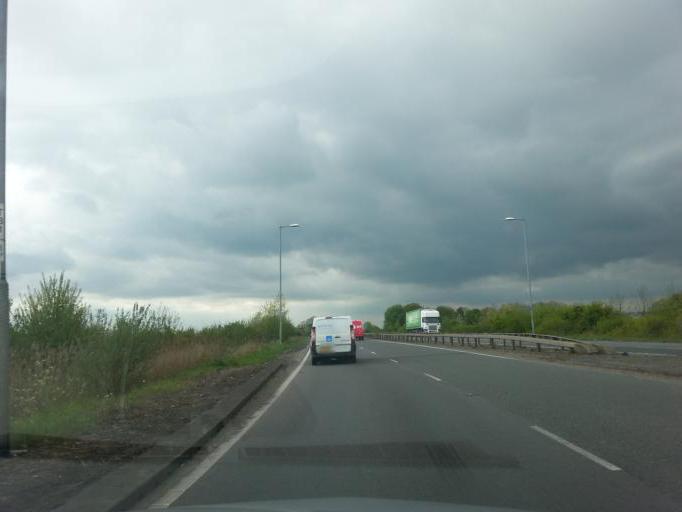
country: GB
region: England
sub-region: Peterborough
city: Thorney
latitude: 52.6216
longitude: -0.0573
